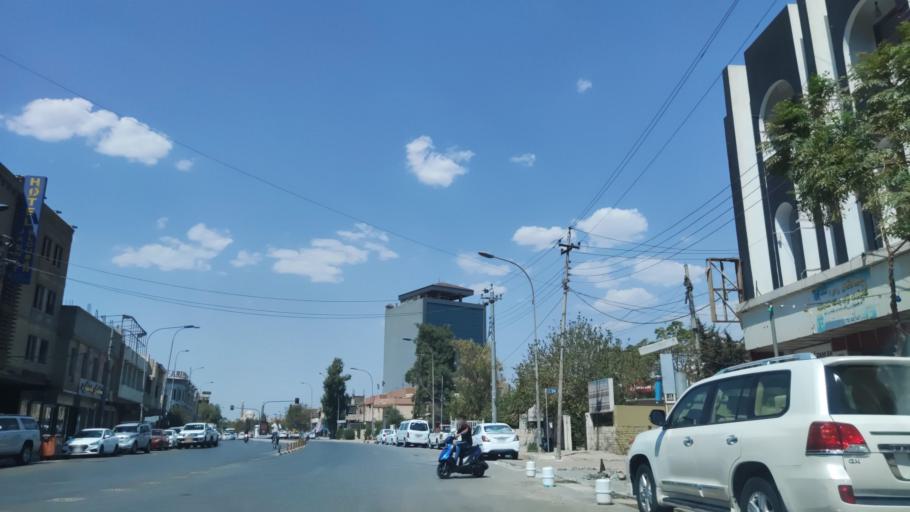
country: IQ
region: Arbil
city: Erbil
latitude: 36.1888
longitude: 44.0195
